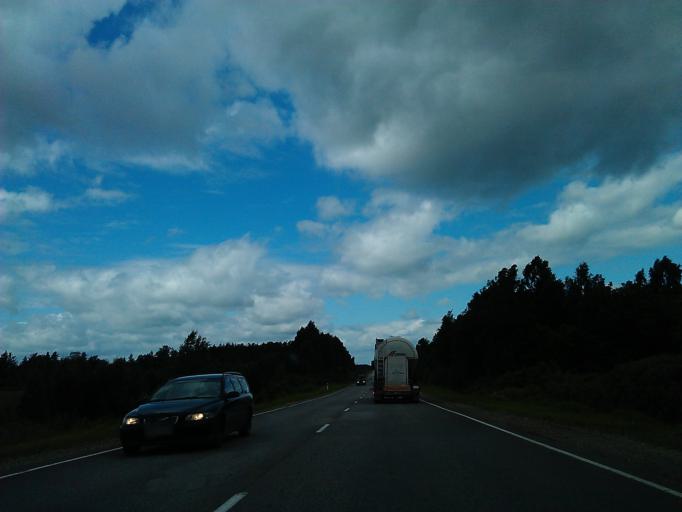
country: LV
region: Tukuma Rajons
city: Tukums
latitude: 56.9348
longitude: 23.1921
